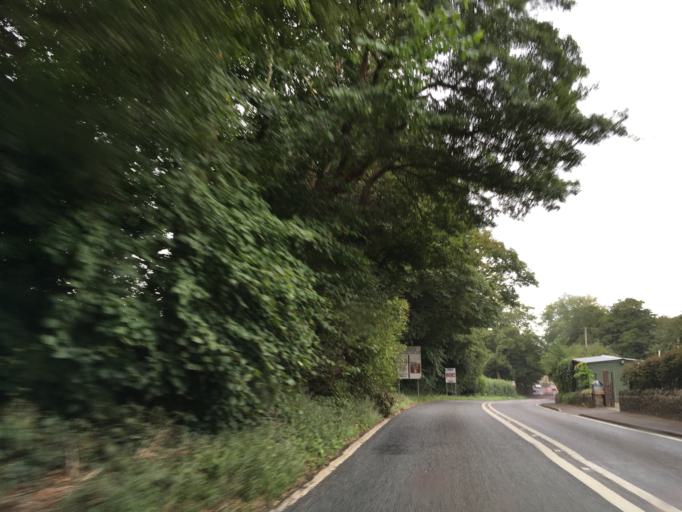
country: GB
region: England
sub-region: Somerset
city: Wells
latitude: 51.2168
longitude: -2.6445
